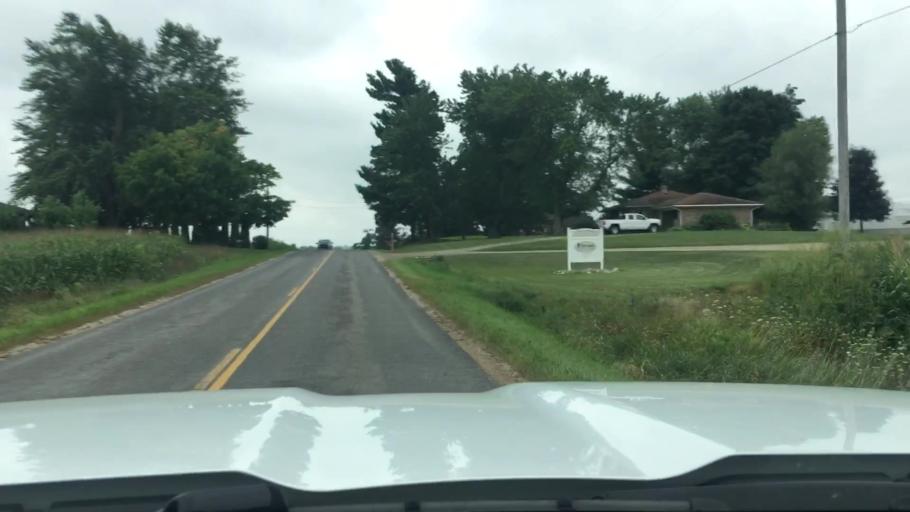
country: US
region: Michigan
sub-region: Ottawa County
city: Hudsonville
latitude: 42.7867
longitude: -85.8616
